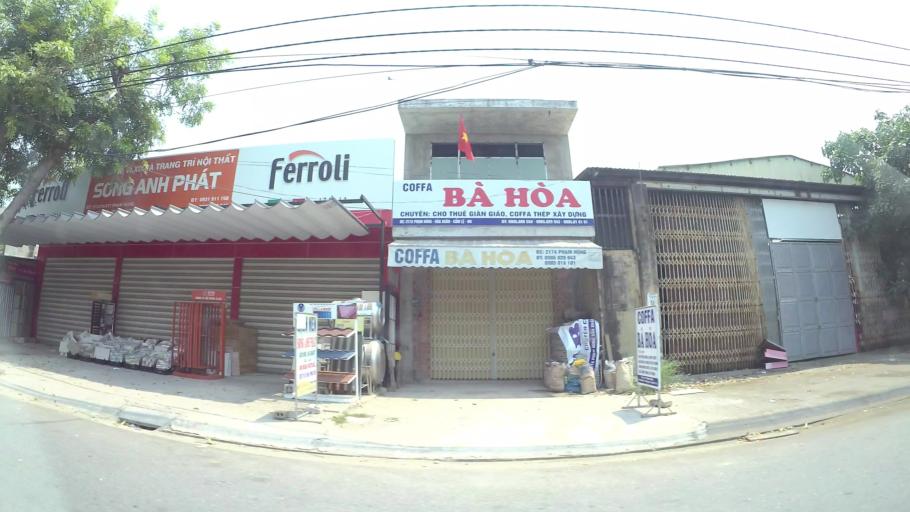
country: VN
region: Da Nang
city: Cam Le
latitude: 15.9904
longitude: 108.2077
